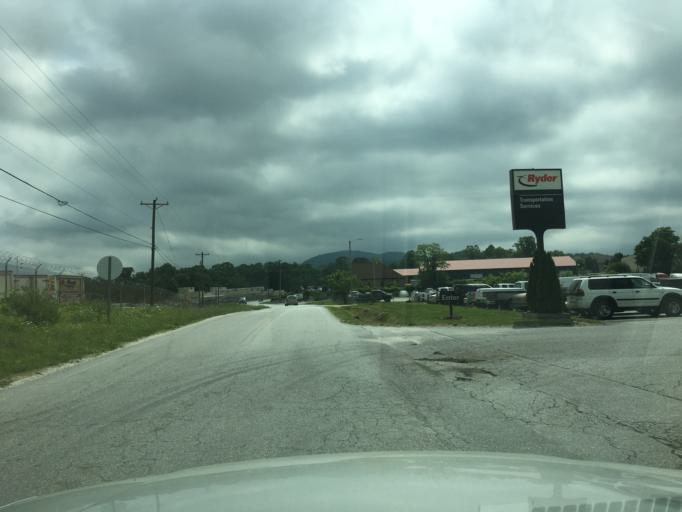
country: US
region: North Carolina
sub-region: Henderson County
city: Fletcher
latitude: 35.4130
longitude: -82.5071
